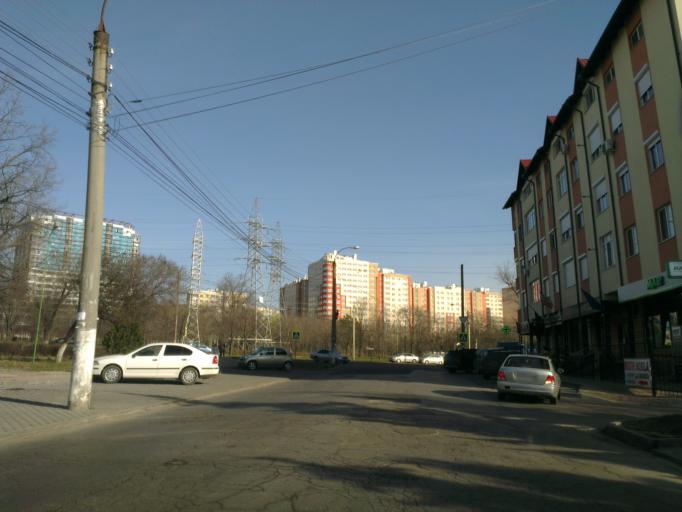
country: MD
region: Chisinau
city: Chisinau
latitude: 47.0306
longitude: 28.8841
